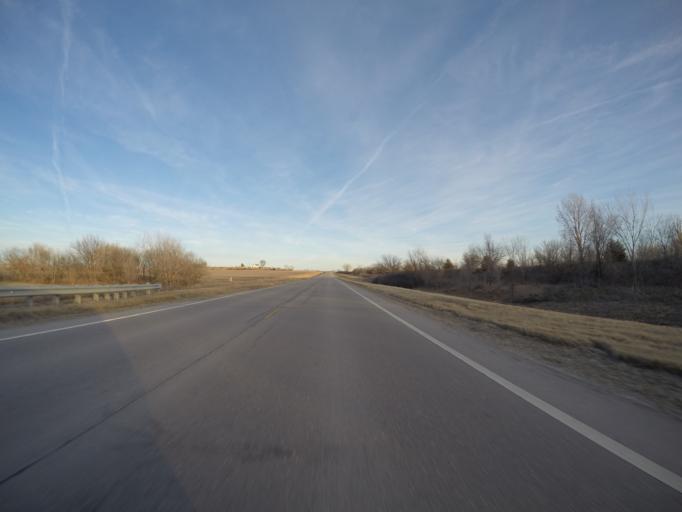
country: US
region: Kansas
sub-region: Dickinson County
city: Herington
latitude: 38.6623
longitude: -96.8625
